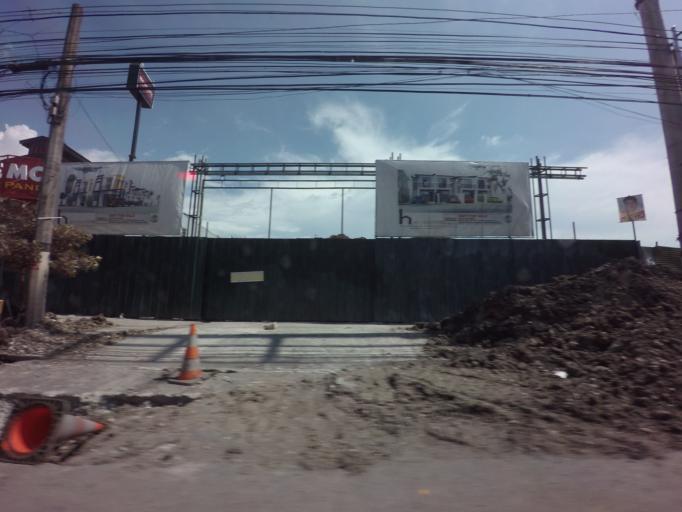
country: PH
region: Calabarzon
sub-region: Province of Rizal
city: Las Pinas
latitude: 14.4468
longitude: 120.9879
